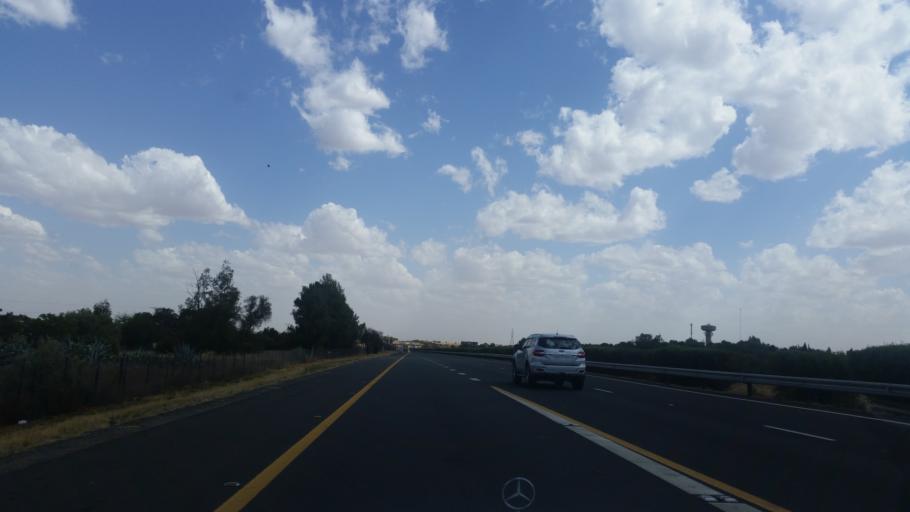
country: ZA
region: Orange Free State
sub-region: Mangaung Metropolitan Municipality
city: Bloemfontein
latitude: -29.0779
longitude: 26.1800
